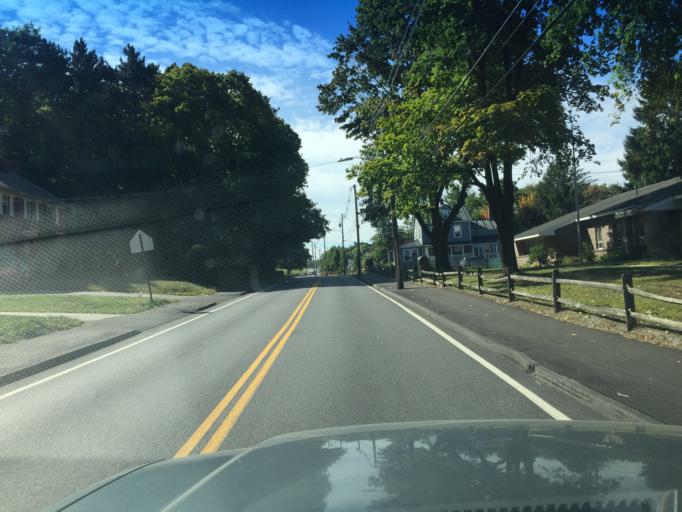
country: US
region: Massachusetts
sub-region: Middlesex County
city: Hudson
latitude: 42.3846
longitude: -71.5642
